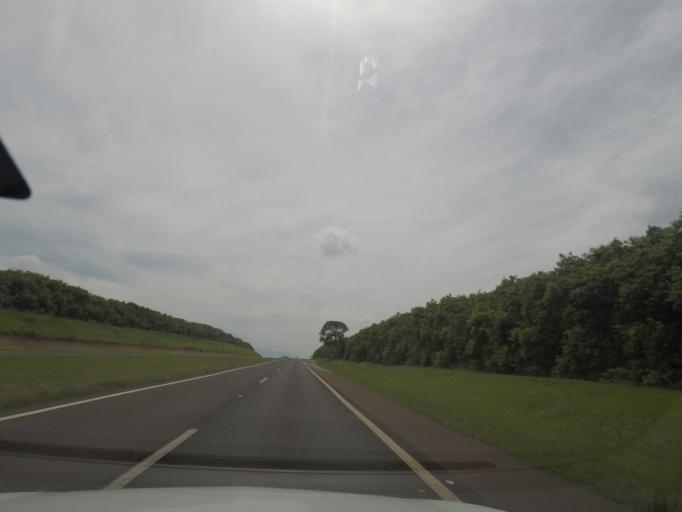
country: BR
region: Sao Paulo
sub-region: Bebedouro
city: Bebedouro
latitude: -21.0137
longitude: -48.4262
